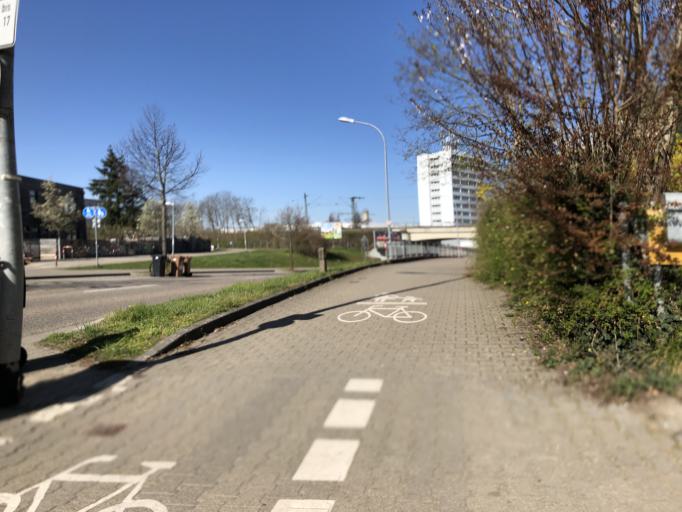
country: DE
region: Baden-Wuerttemberg
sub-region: Freiburg Region
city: Merzhausen
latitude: 47.9780
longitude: 7.8246
